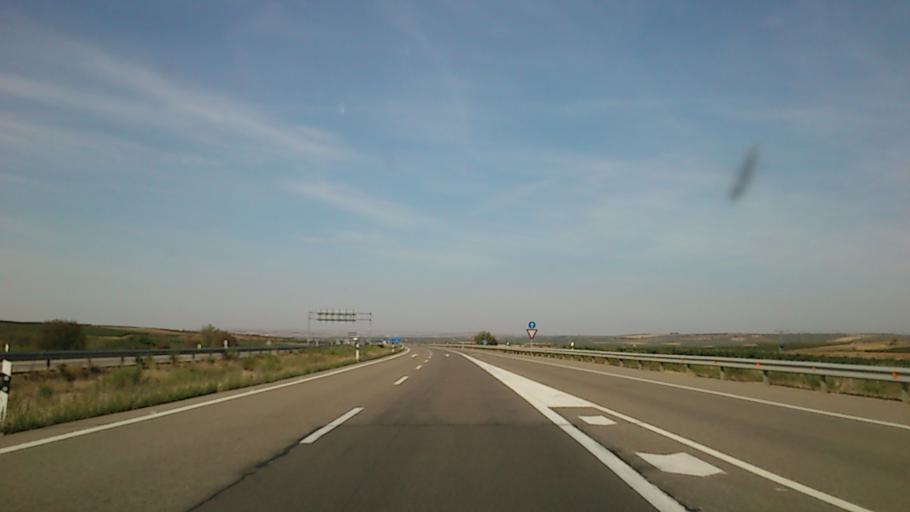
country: ES
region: Aragon
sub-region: Provincia de Zaragoza
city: Paniza
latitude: 41.3020
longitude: -1.2139
